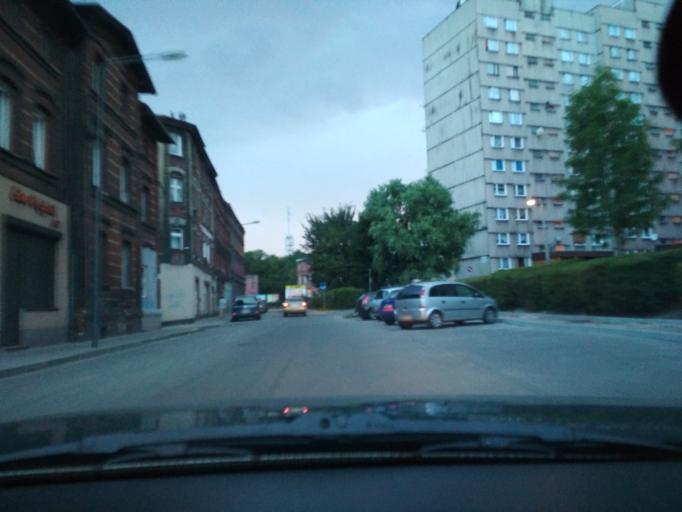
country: PL
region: Silesian Voivodeship
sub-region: Swietochlowice
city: Swietochlowice
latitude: 50.2928
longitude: 18.9186
